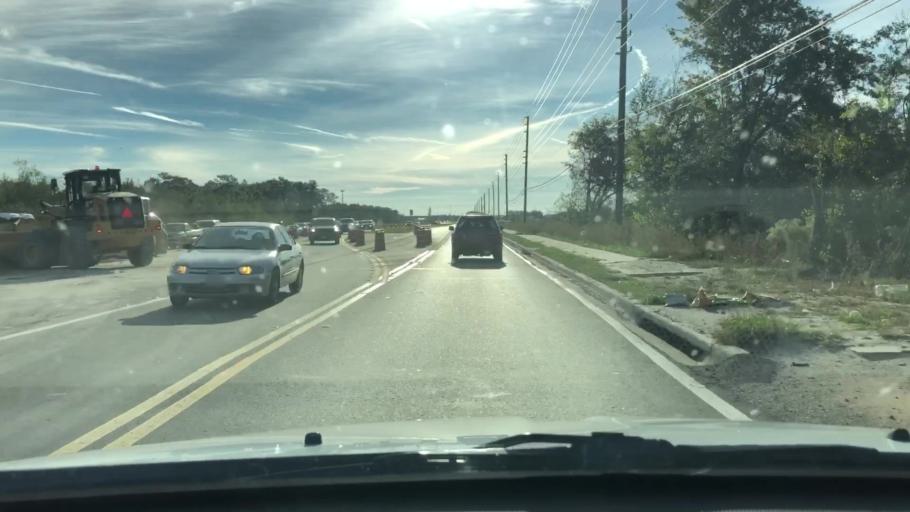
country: US
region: Florida
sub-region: Orange County
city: Meadow Woods
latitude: 28.3905
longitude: -81.3206
